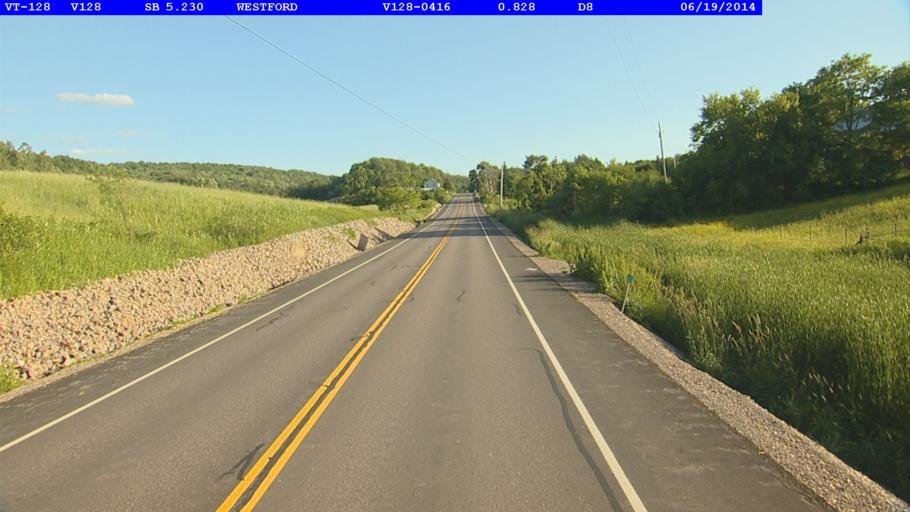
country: US
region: Vermont
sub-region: Chittenden County
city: Jericho
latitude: 44.5701
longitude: -73.0221
